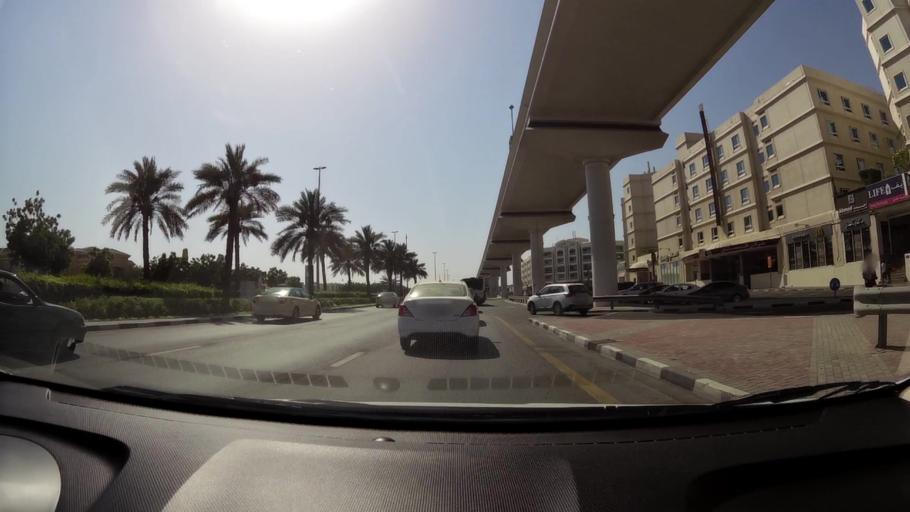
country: AE
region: Ash Shariqah
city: Sharjah
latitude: 25.2741
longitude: 55.3678
